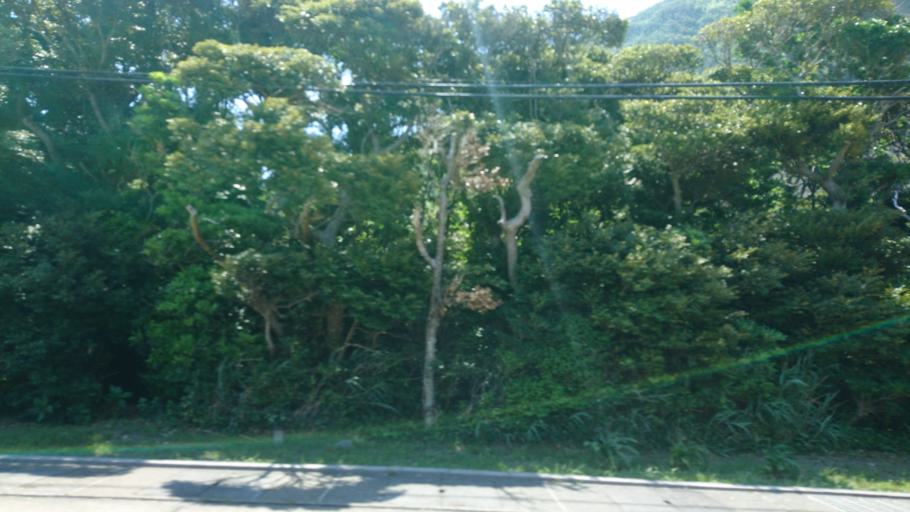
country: JP
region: Shizuoka
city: Shimoda
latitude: 34.3839
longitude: 139.2738
